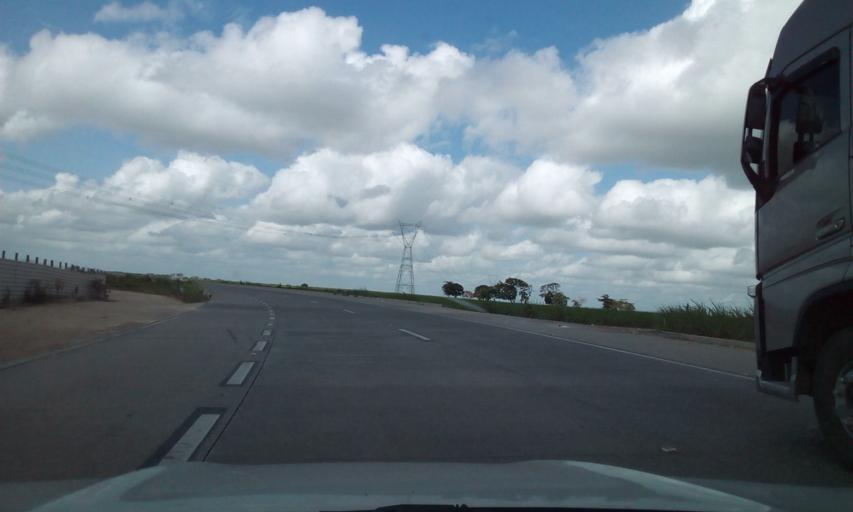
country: BR
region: Alagoas
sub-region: Messias
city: Messias
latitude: -9.4020
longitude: -35.8375
